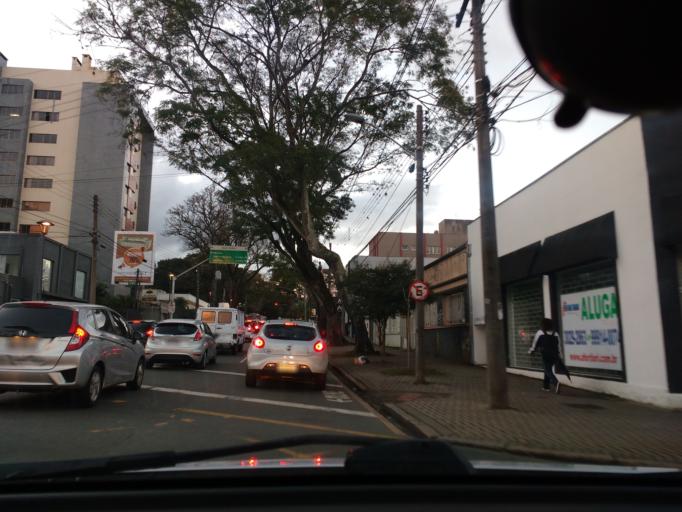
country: BR
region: Parana
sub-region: Curitiba
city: Curitiba
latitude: -25.4296
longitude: -49.2841
